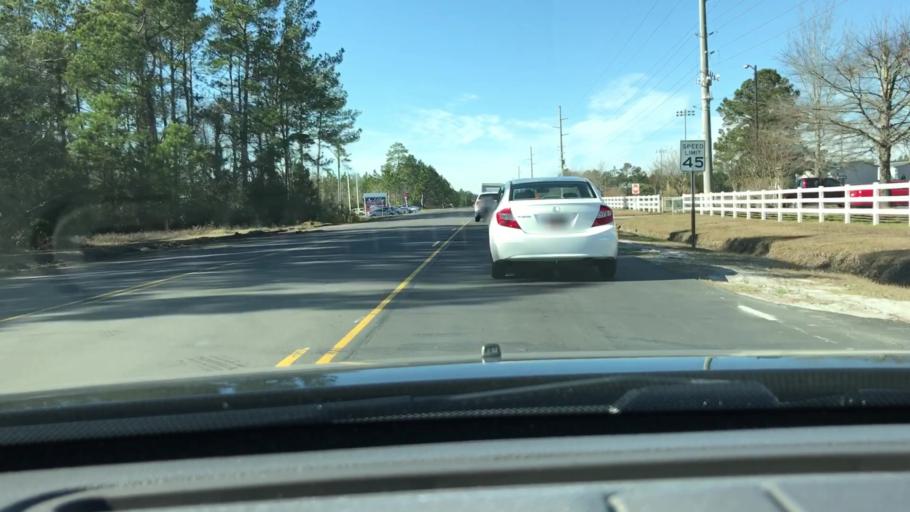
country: US
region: North Carolina
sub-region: Brunswick County
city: Shallotte
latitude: 33.9787
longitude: -78.4098
